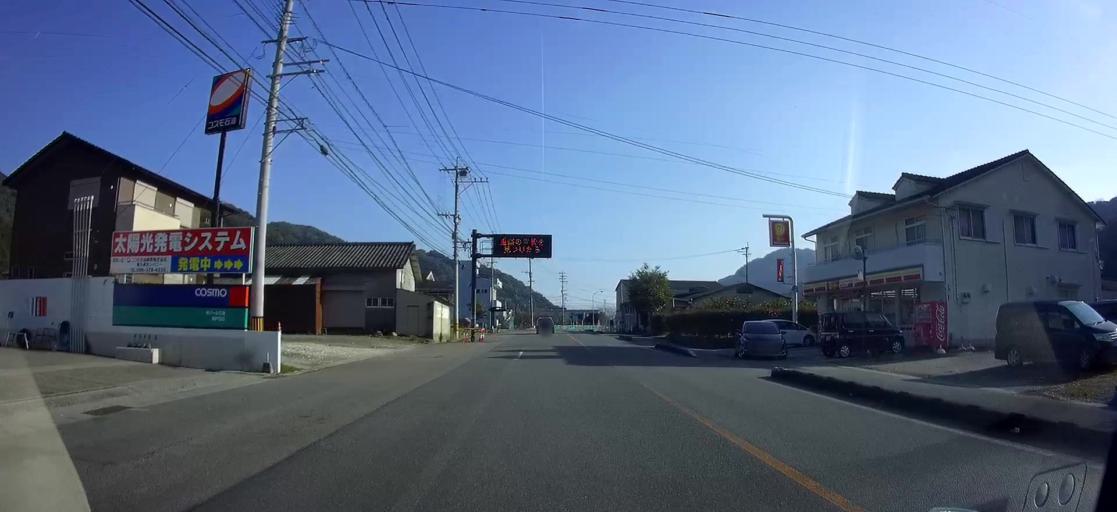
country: JP
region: Kumamoto
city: Hondo
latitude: 32.4293
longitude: 130.4015
